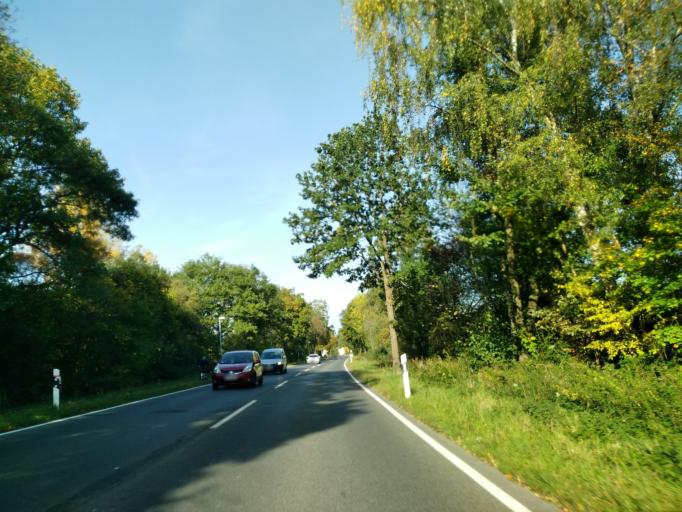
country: DE
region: North Rhine-Westphalia
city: Sankt Augustin
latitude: 50.7587
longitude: 7.2143
